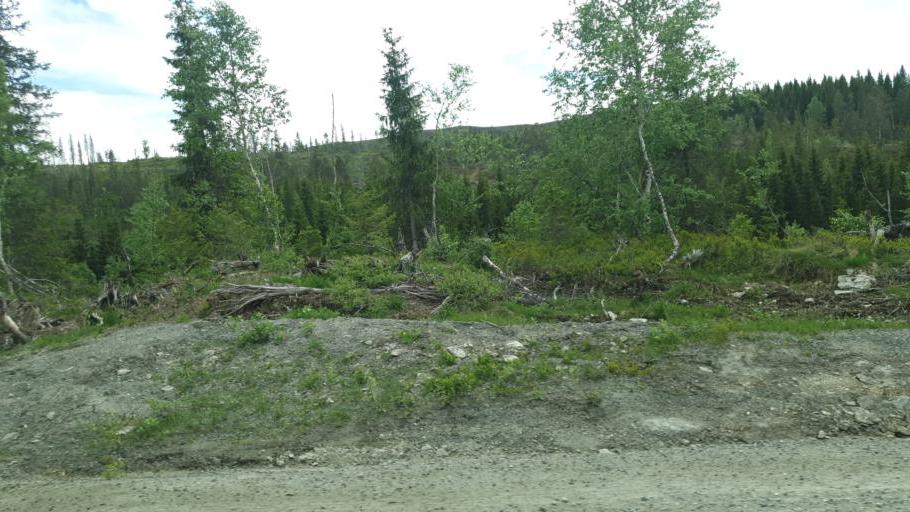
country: NO
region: Sor-Trondelag
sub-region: Trondheim
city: Trondheim
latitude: 63.6813
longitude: 10.3616
